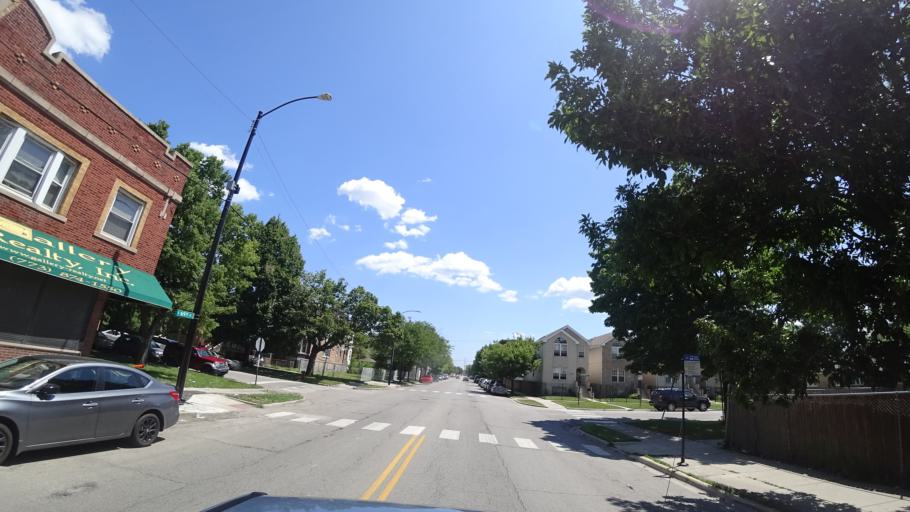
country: US
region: Illinois
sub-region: Cook County
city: Chicago
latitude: 41.7692
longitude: -87.6237
